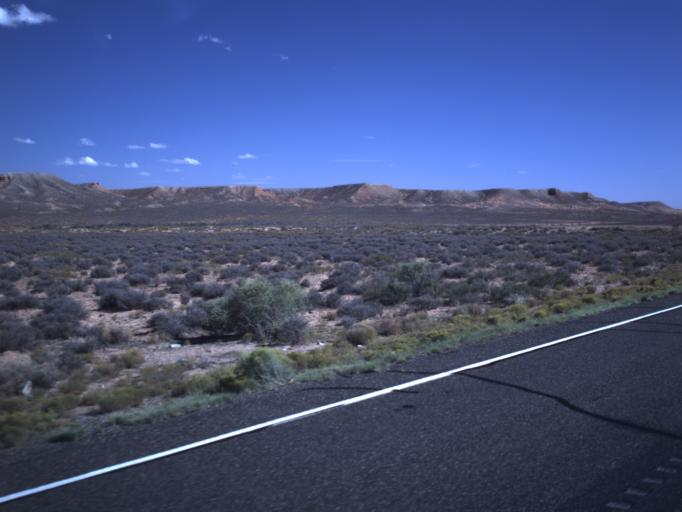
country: US
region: Utah
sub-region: Wayne County
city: Loa
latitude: 38.1017
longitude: -110.6235
